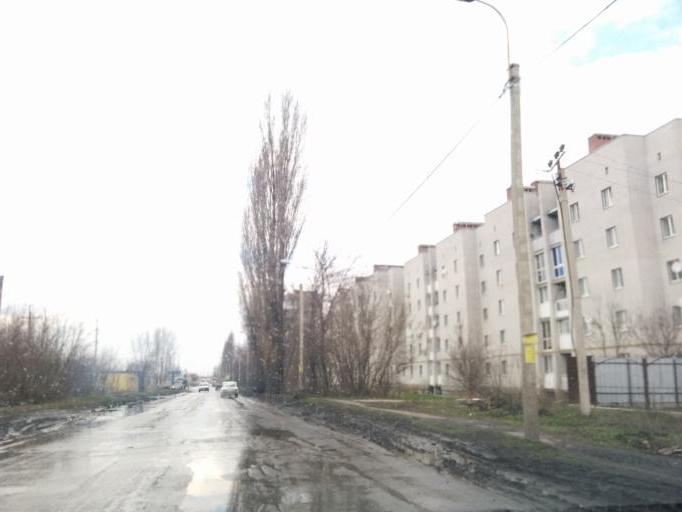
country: RU
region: Rostov
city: Shakhty
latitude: 47.6844
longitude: 40.2724
